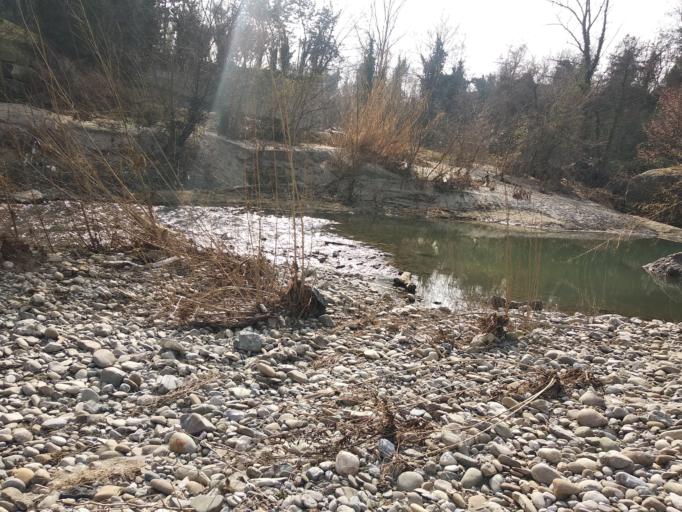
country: IT
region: Emilia-Romagna
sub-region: Provincia di Bologna
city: Ponticella
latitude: 44.4567
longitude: 11.3744
